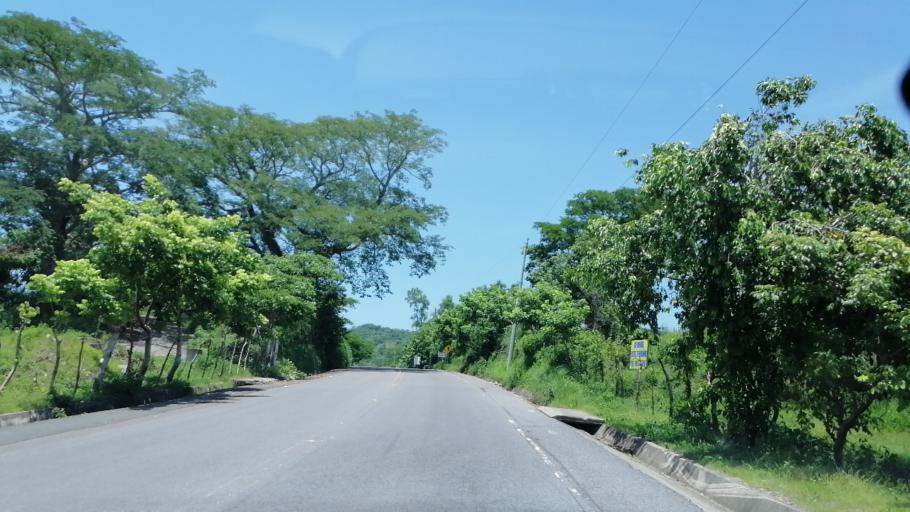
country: SV
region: Chalatenango
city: Chalatenango
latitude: 14.0343
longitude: -88.9628
